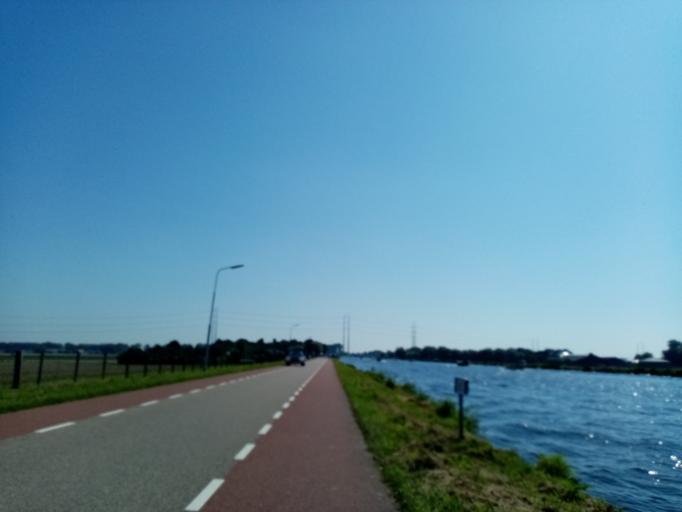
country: NL
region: South Holland
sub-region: Gemeente Kaag en Braassem
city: Oude Wetering
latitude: 52.2176
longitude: 4.5912
